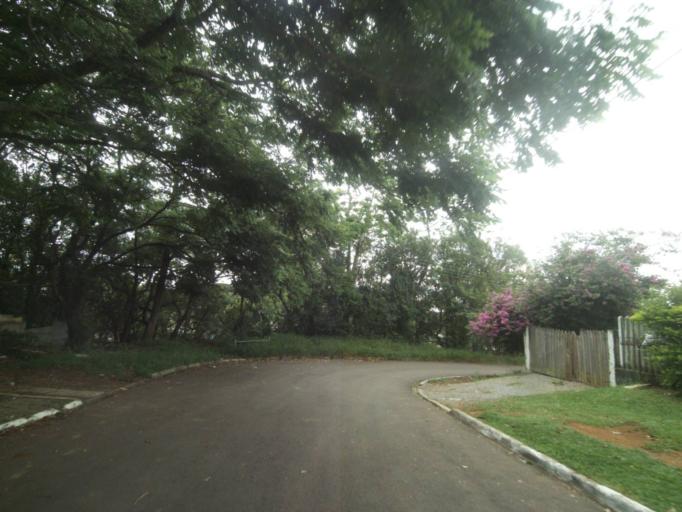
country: BR
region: Parana
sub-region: Curitiba
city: Curitiba
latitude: -25.3863
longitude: -49.2887
